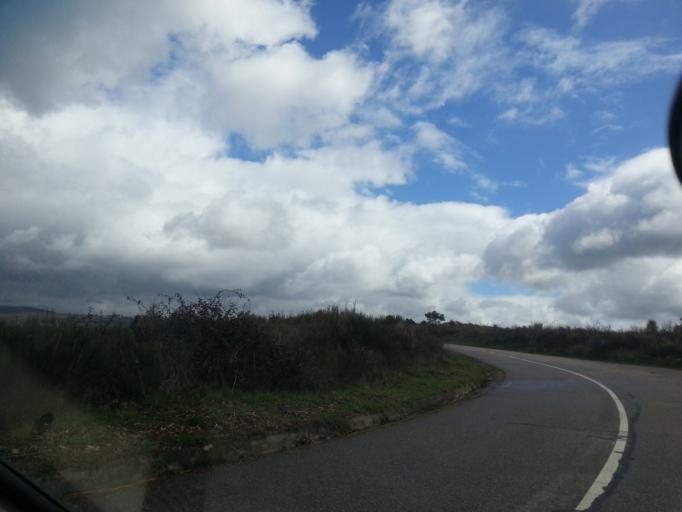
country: PT
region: Guarda
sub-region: Fornos de Algodres
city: Fornos de Algodres
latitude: 40.5931
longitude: -7.5003
